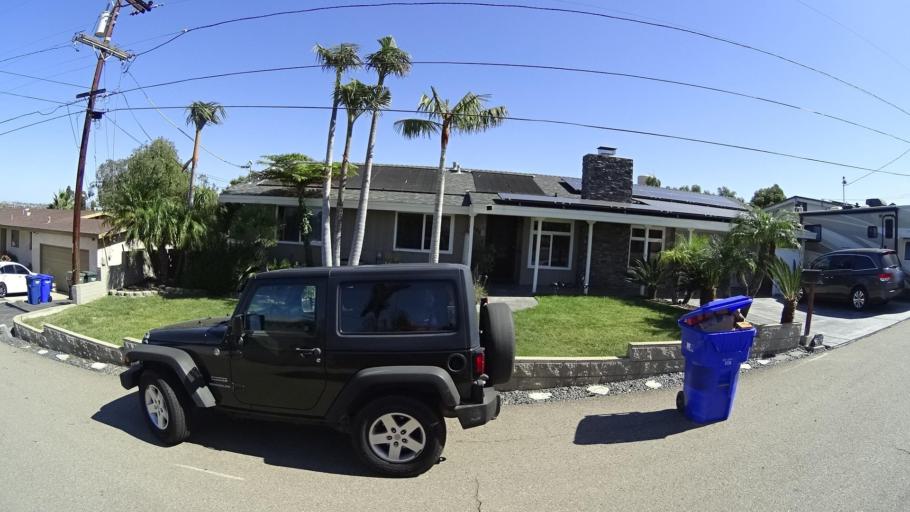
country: US
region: California
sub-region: San Diego County
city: Bonita
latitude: 32.6463
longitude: -117.0501
